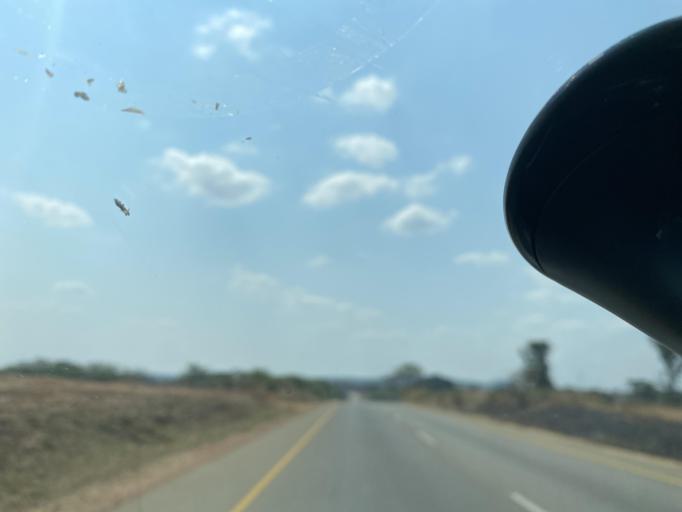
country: ZM
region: Lusaka
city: Chongwe
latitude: -15.5578
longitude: 28.6838
